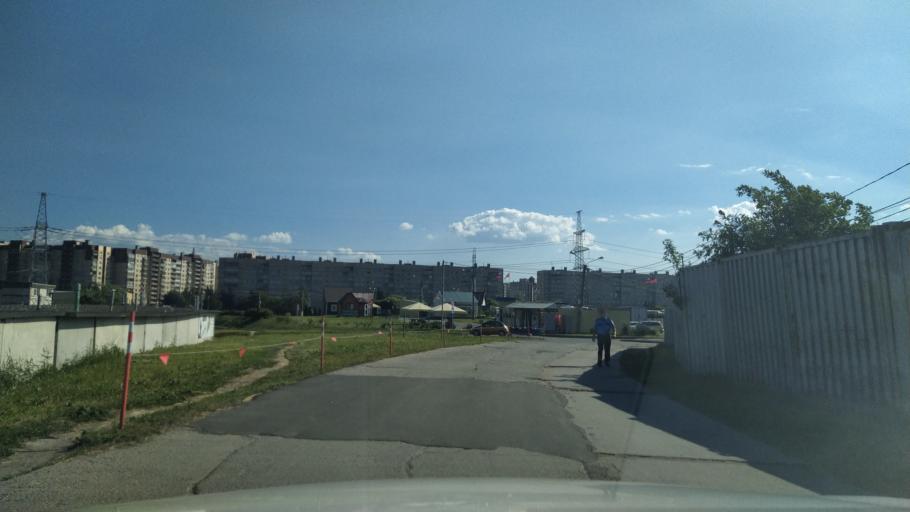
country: RU
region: St.-Petersburg
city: Uritsk
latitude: 59.8628
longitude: 30.2121
